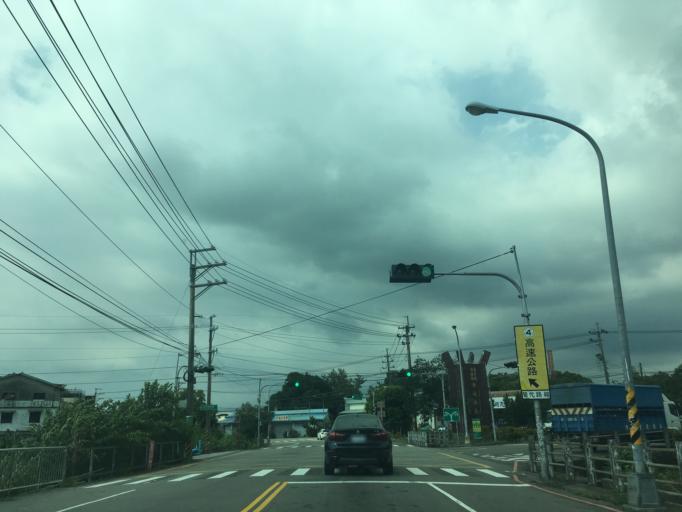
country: TW
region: Taiwan
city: Fengyuan
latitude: 24.2437
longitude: 120.8104
